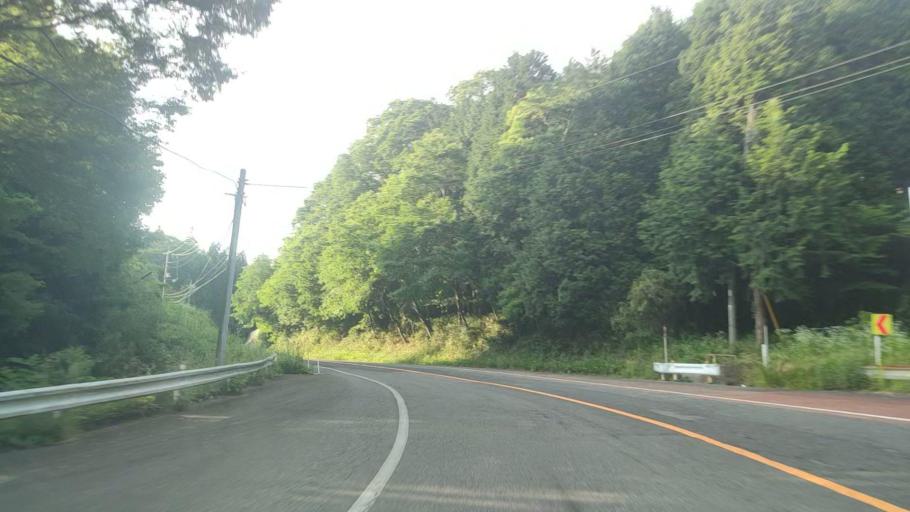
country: JP
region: Tottori
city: Kurayoshi
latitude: 35.2833
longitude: 133.6376
